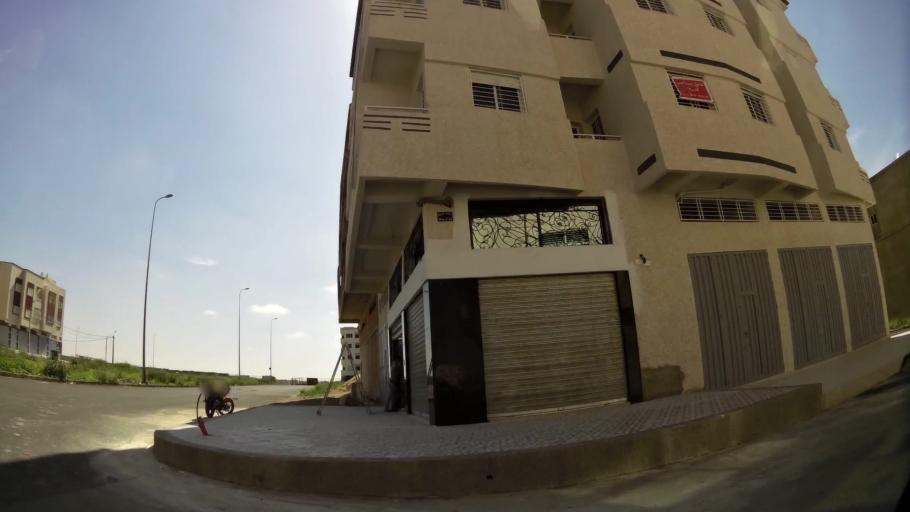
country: MA
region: Fes-Boulemane
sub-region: Fes
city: Fes
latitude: 34.0095
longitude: -5.0352
